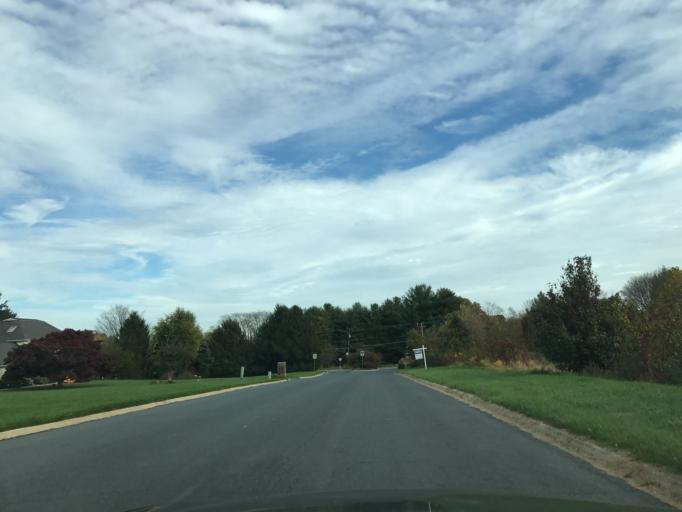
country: US
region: Maryland
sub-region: Harford County
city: Pleasant Hills
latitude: 39.4834
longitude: -76.3759
